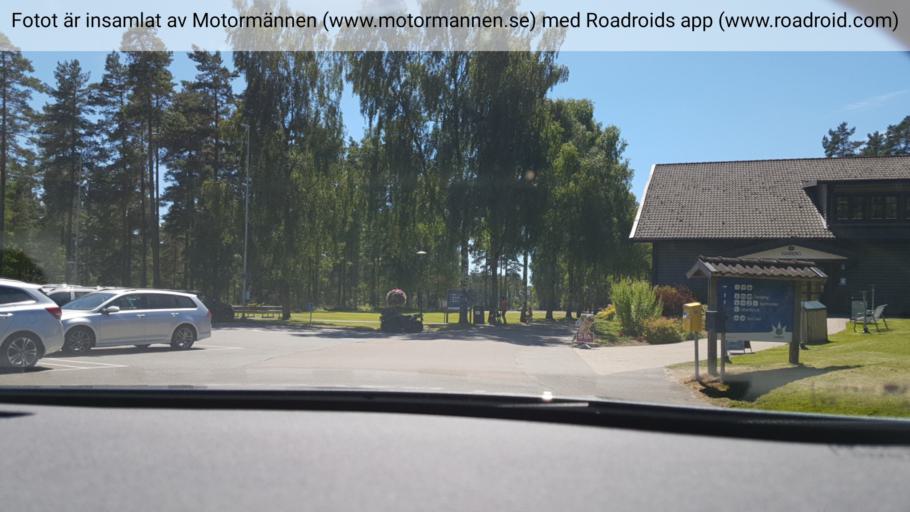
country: SE
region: Joenkoeping
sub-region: Gnosjo Kommun
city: Gnosjoe
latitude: 57.4370
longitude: 13.6246
